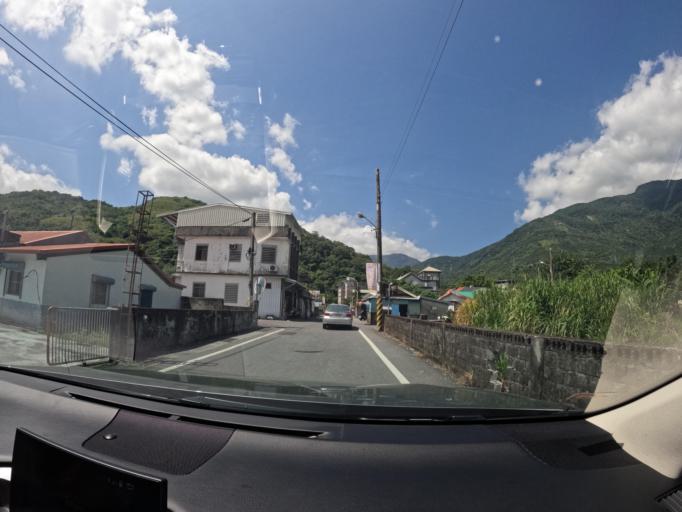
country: TW
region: Taiwan
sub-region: Hualien
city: Hualian
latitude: 23.7146
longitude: 121.4122
